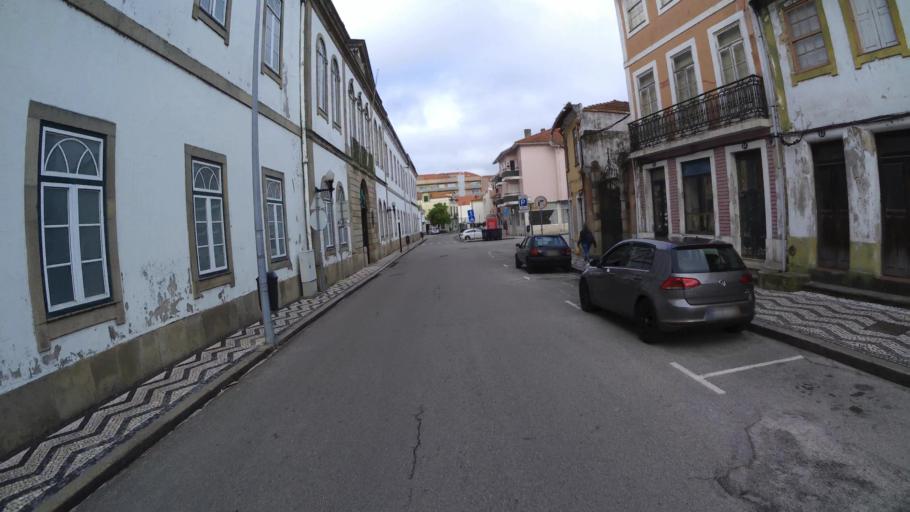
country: PT
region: Aveiro
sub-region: Aveiro
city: Aveiro
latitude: 40.6454
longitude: -8.6462
